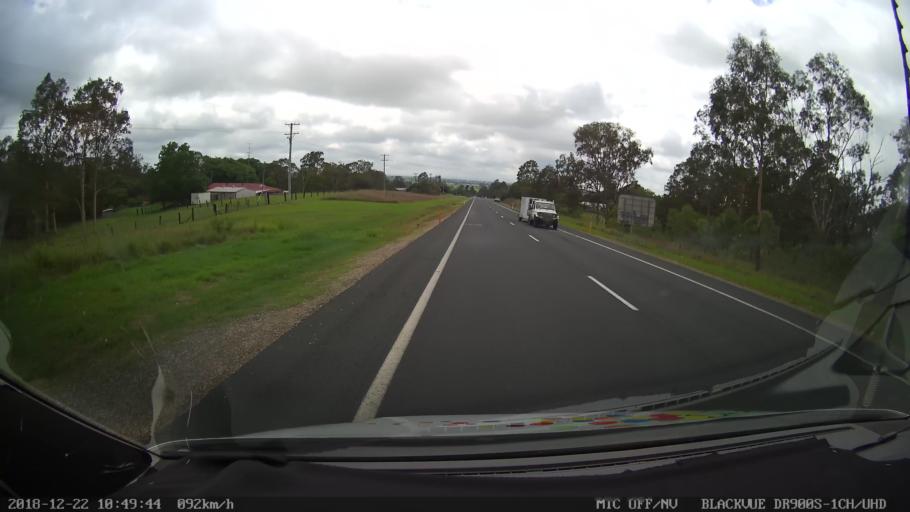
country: AU
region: New South Wales
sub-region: Clarence Valley
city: South Grafton
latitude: -29.6836
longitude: 152.8723
